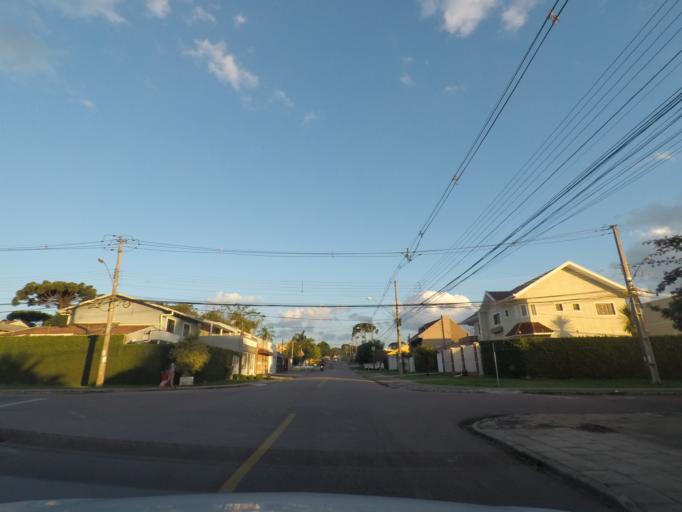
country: BR
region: Parana
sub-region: Sao Jose Dos Pinhais
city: Sao Jose dos Pinhais
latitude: -25.4976
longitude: -49.2562
